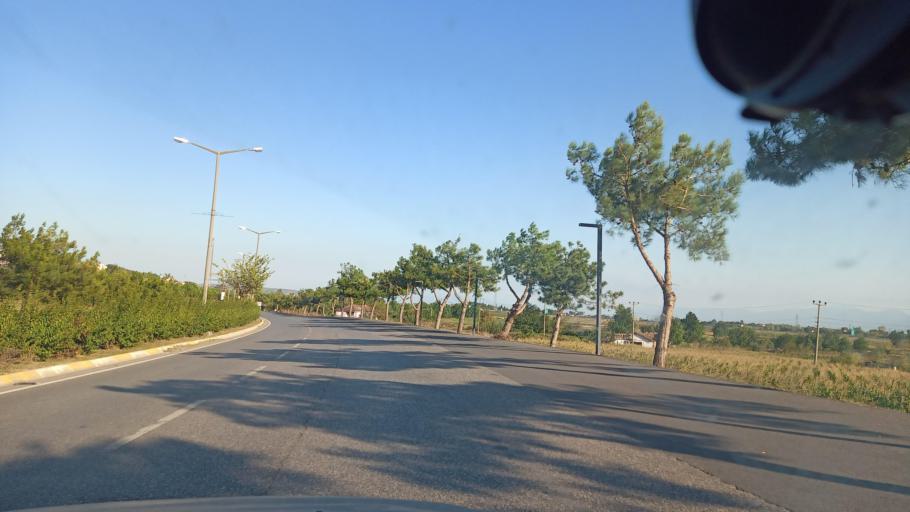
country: TR
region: Sakarya
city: Kazimpasa
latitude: 40.8497
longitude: 30.3186
